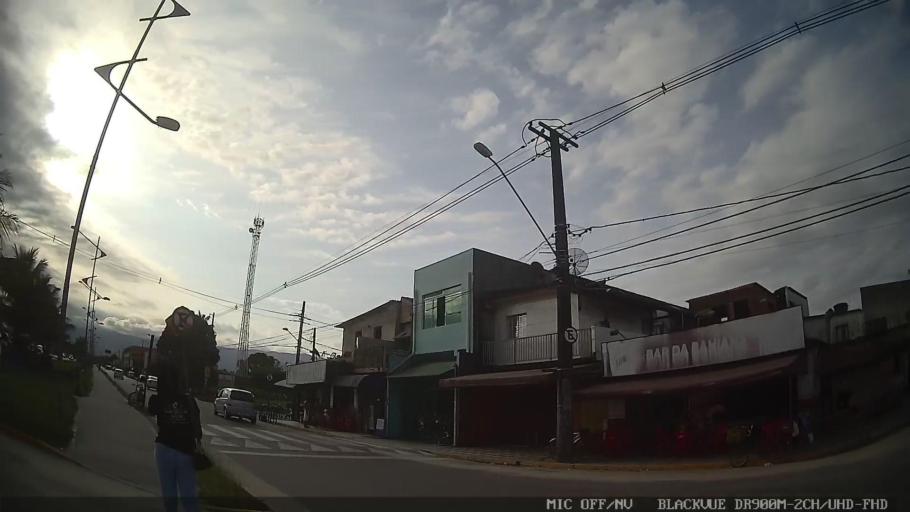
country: BR
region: Sao Paulo
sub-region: Bertioga
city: Bertioga
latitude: -23.8059
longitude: -46.0545
